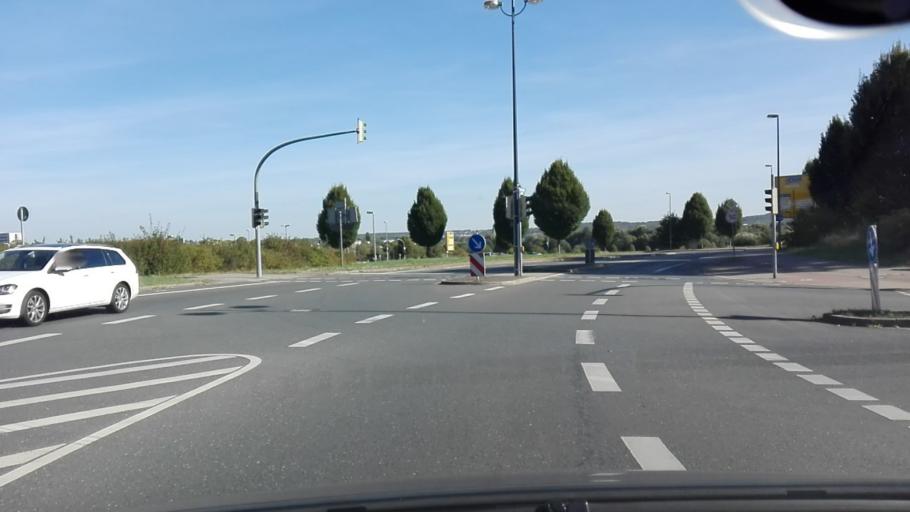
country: DE
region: North Rhine-Westphalia
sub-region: Regierungsbezirk Arnsberg
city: Dortmund
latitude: 51.5068
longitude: 7.5338
